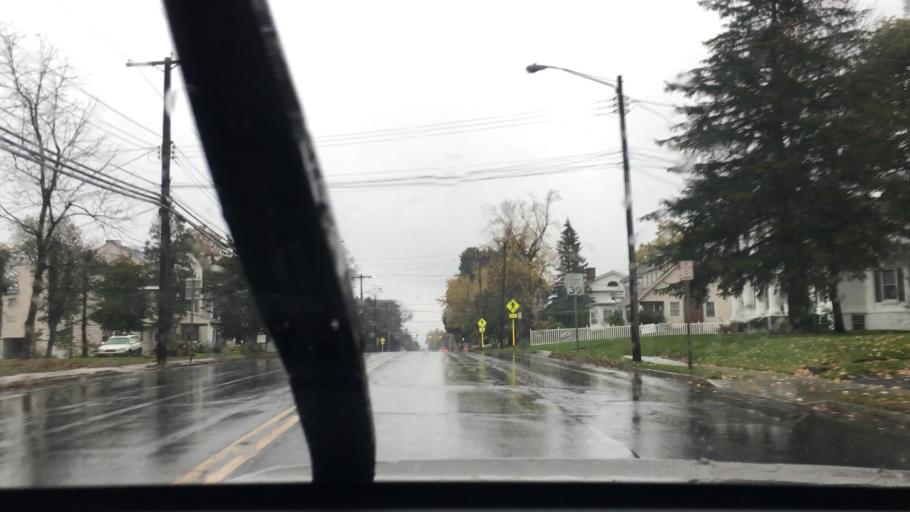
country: US
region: New York
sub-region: Cayuga County
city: Auburn
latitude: 42.9382
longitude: -76.5666
